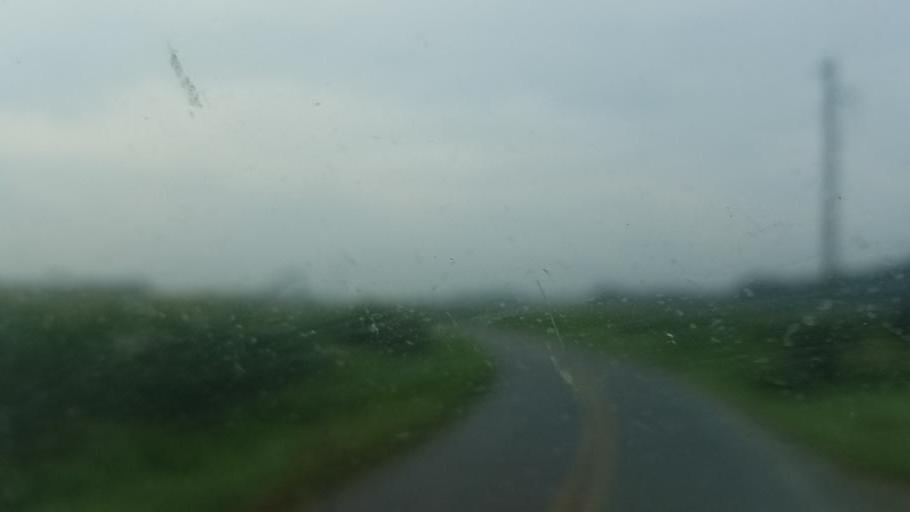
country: US
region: Maryland
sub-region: Wicomico County
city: Pittsville
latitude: 38.4360
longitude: -75.3283
